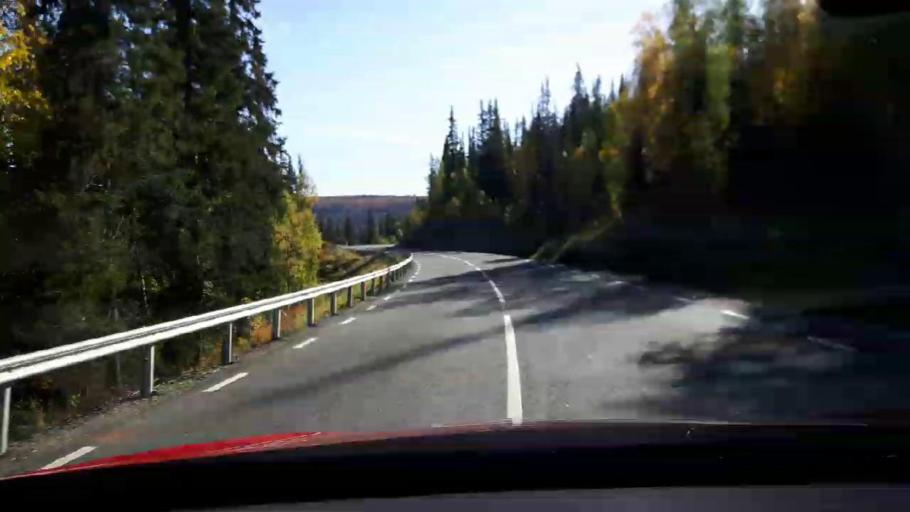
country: NO
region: Nord-Trondelag
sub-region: Royrvik
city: Royrvik
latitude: 64.8580
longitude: 14.1798
